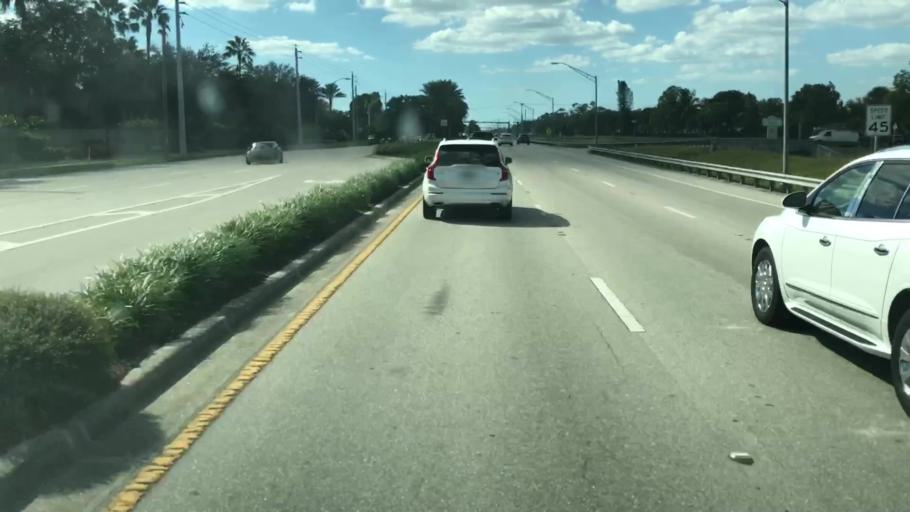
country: US
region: Florida
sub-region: Collier County
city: Vineyards
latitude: 26.2731
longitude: -81.7014
